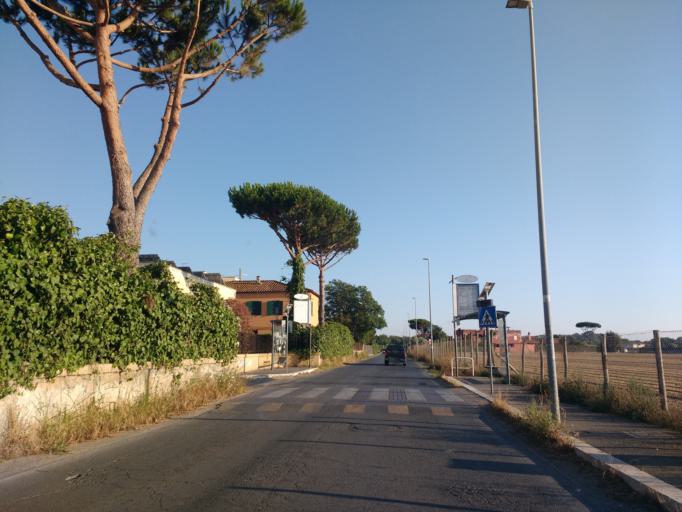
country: IT
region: Latium
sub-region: Citta metropolitana di Roma Capitale
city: Fregene
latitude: 41.8538
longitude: 12.2185
